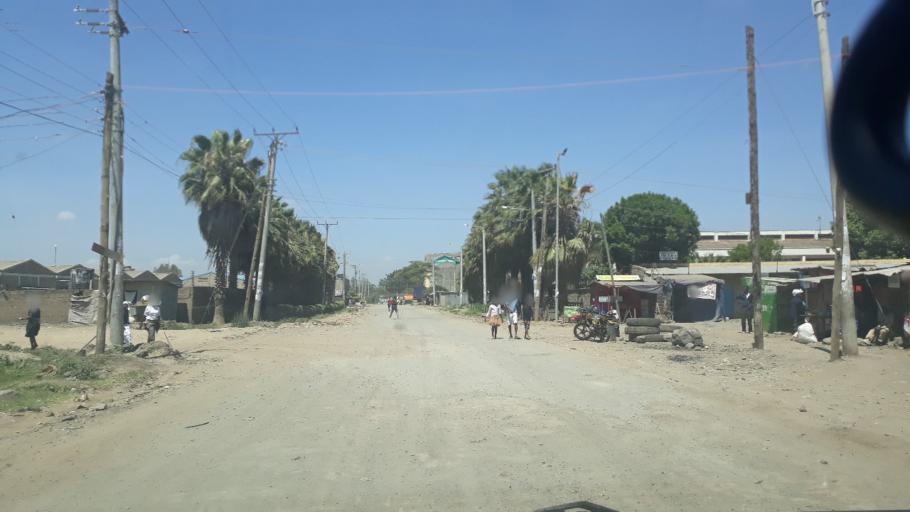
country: KE
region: Nairobi Area
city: Pumwani
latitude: -1.3183
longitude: 36.9059
